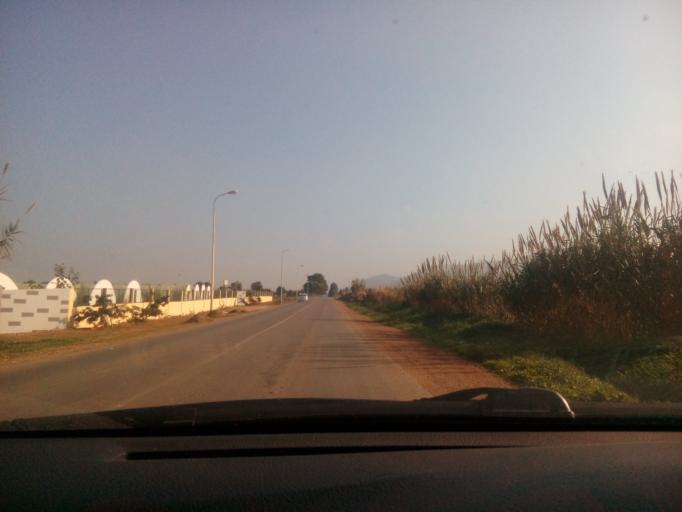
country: DZ
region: Oran
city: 'Ain el Turk
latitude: 35.6998
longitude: -0.8796
